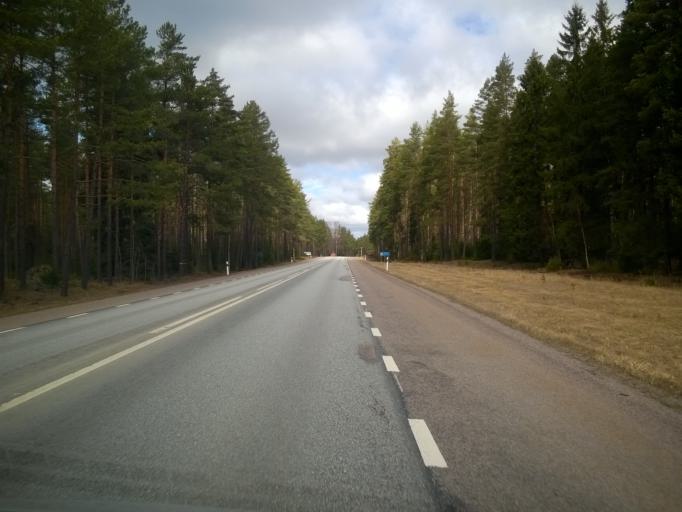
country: SE
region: Uppsala
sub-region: Tierps Kommun
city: Tierp
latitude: 60.1856
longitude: 17.4784
